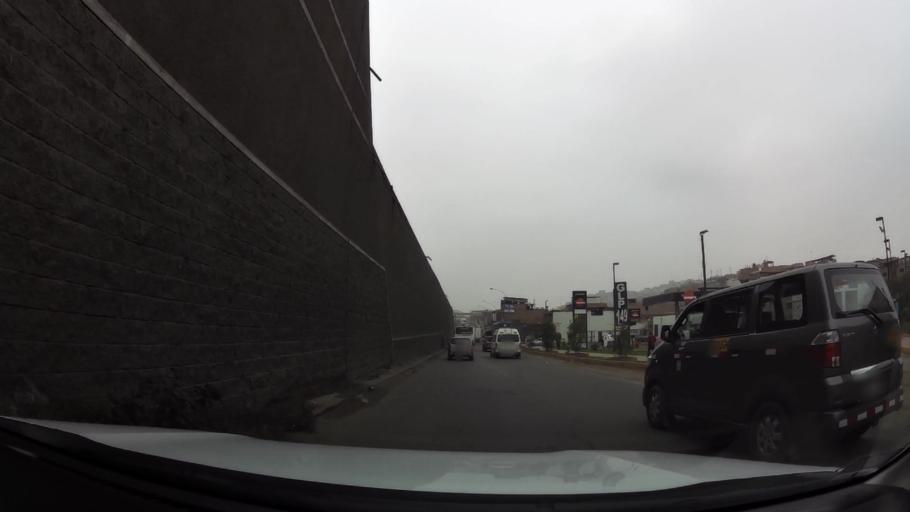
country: PE
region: Lima
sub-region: Lima
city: Surco
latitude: -12.1610
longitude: -76.9565
